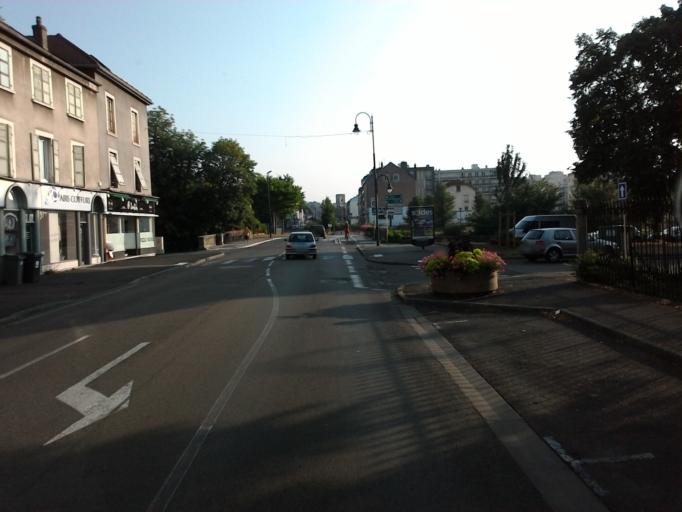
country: FR
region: Franche-Comte
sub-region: Departement de la Haute-Saone
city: Navenne
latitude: 47.6162
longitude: 6.1530
